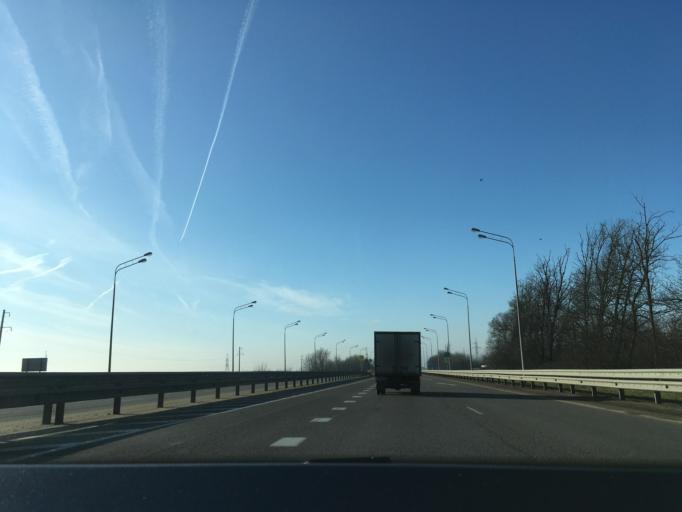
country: RU
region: Krasnodarskiy
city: Agronom
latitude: 45.1757
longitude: 39.1032
